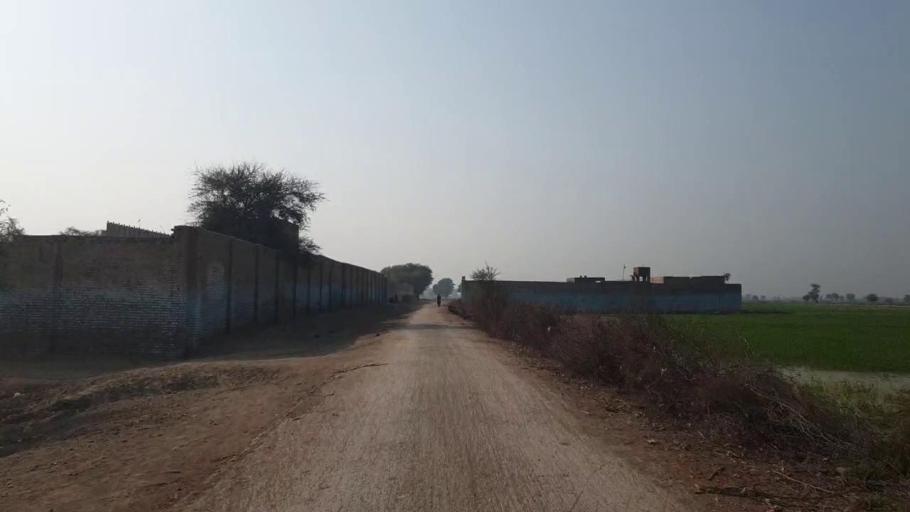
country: PK
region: Sindh
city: Shahdadpur
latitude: 25.9786
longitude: 68.5645
